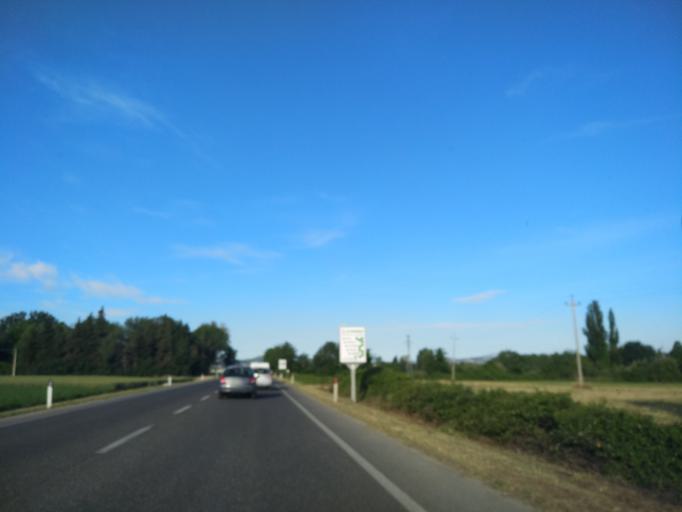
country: IT
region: The Marches
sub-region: Provincia di Pesaro e Urbino
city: Villa Ceccolini
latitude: 43.8723
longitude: 12.8377
